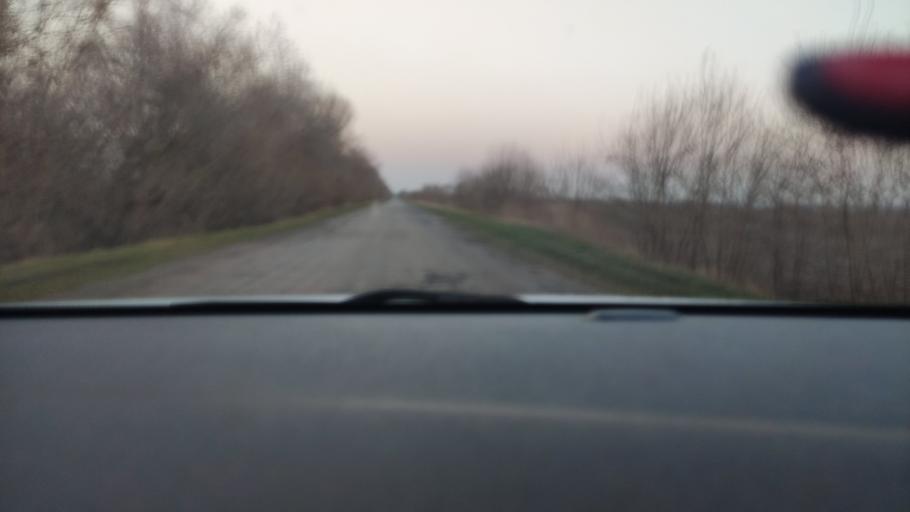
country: RU
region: Voronezj
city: Uryv-Pokrovka
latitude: 51.1420
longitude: 39.0727
